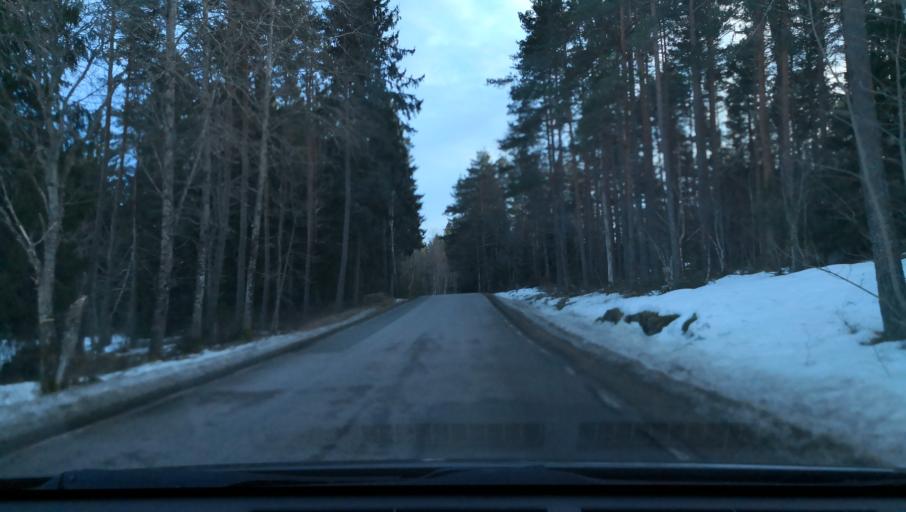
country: SE
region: Uppsala
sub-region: Osthammars Kommun
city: Osterbybruk
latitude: 60.2242
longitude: 17.9188
